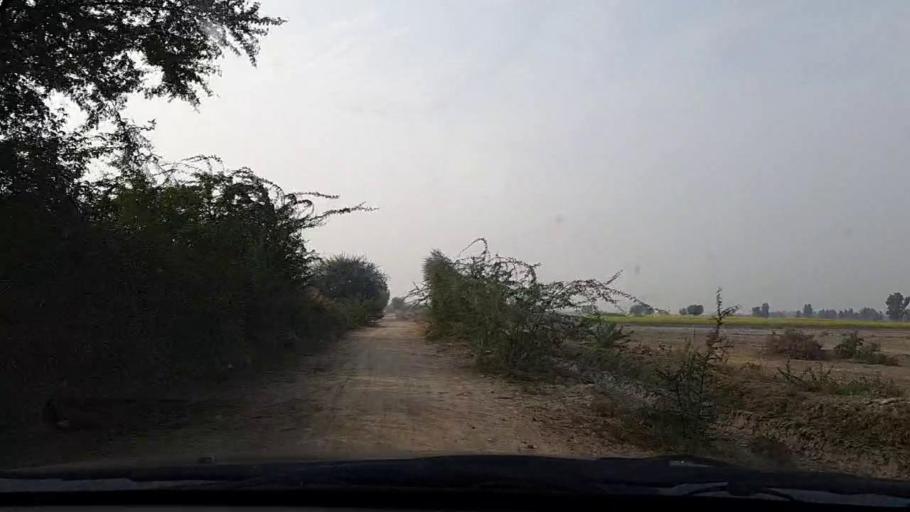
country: PK
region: Sindh
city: Pithoro
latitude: 25.7450
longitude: 69.3847
